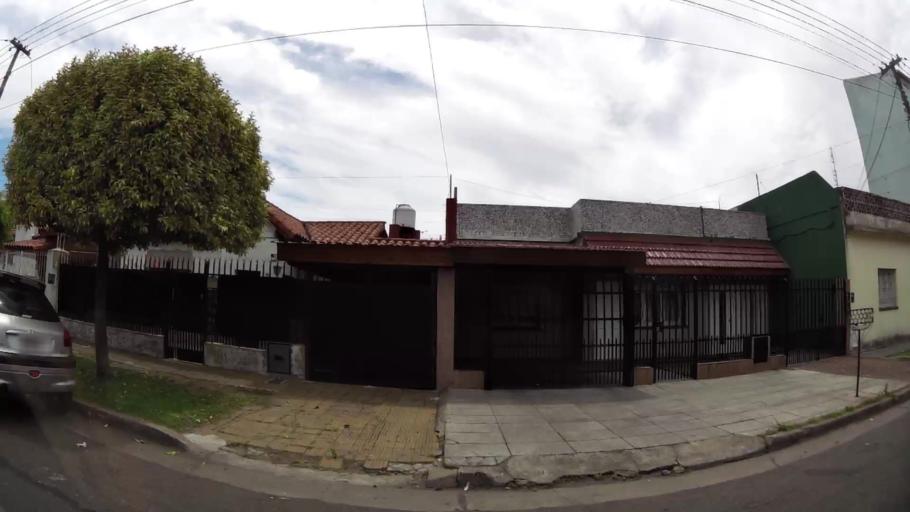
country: AR
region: Buenos Aires
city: San Justo
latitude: -34.6734
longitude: -58.5468
